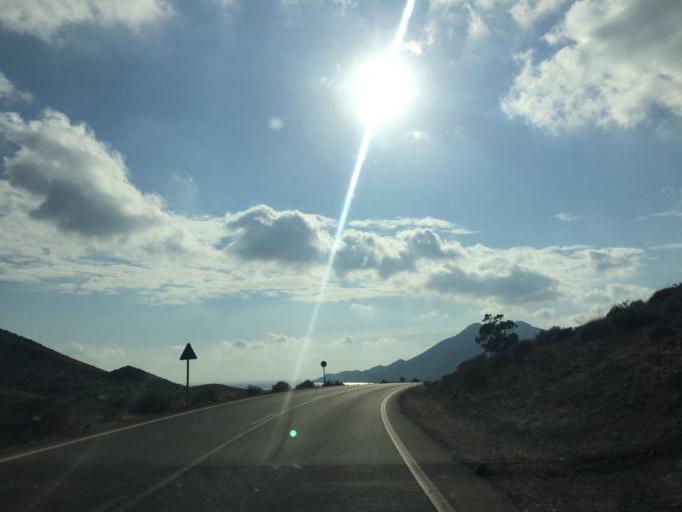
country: ES
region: Andalusia
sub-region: Provincia de Almeria
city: San Jose
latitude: 36.8245
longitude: -2.0475
